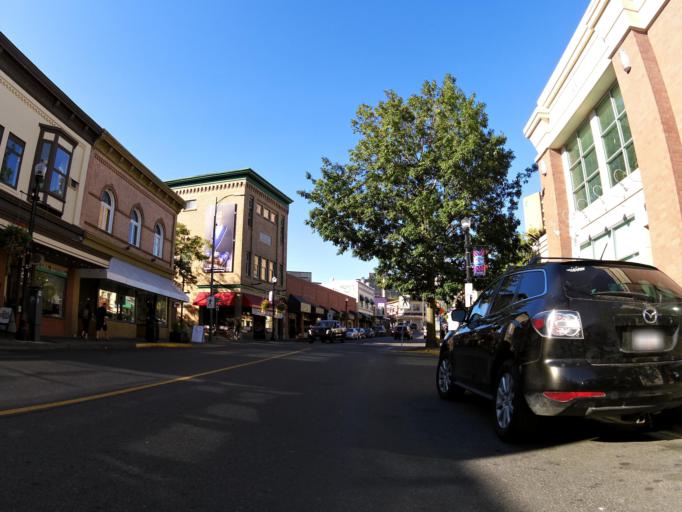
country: CA
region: British Columbia
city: Nanaimo
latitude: 49.1653
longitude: -123.9368
